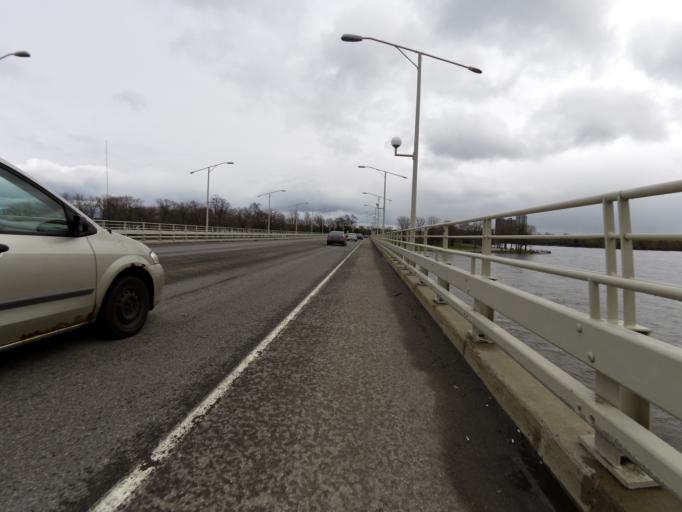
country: CA
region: Ontario
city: Ottawa
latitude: 45.4095
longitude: -75.7592
